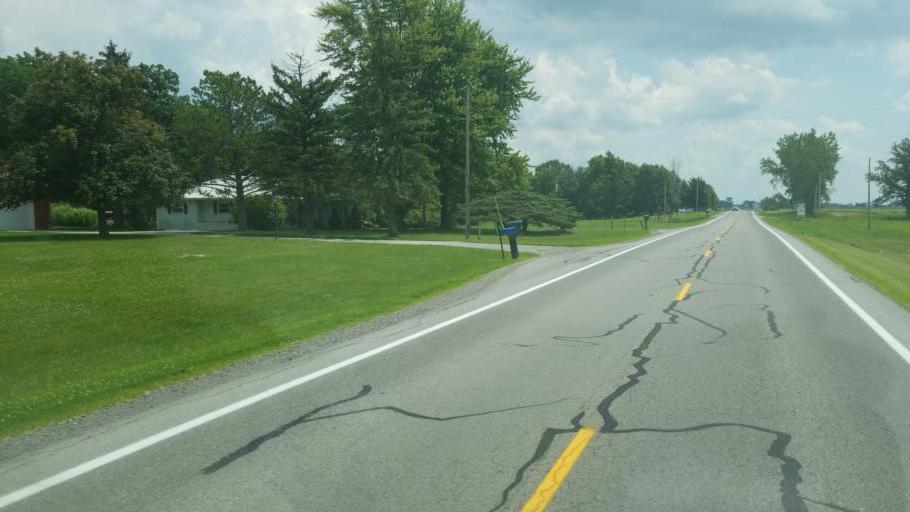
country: US
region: Ohio
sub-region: Hardin County
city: Kenton
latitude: 40.5894
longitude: -83.5932
